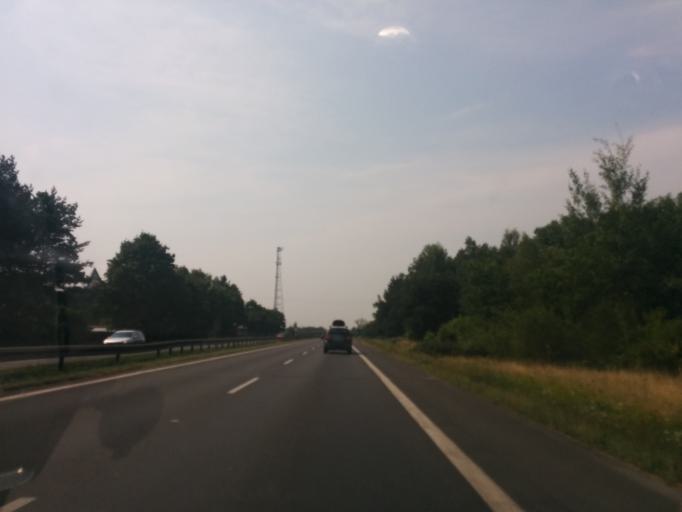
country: PL
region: Lodz Voivodeship
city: Zabia Wola
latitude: 52.0300
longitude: 20.6759
